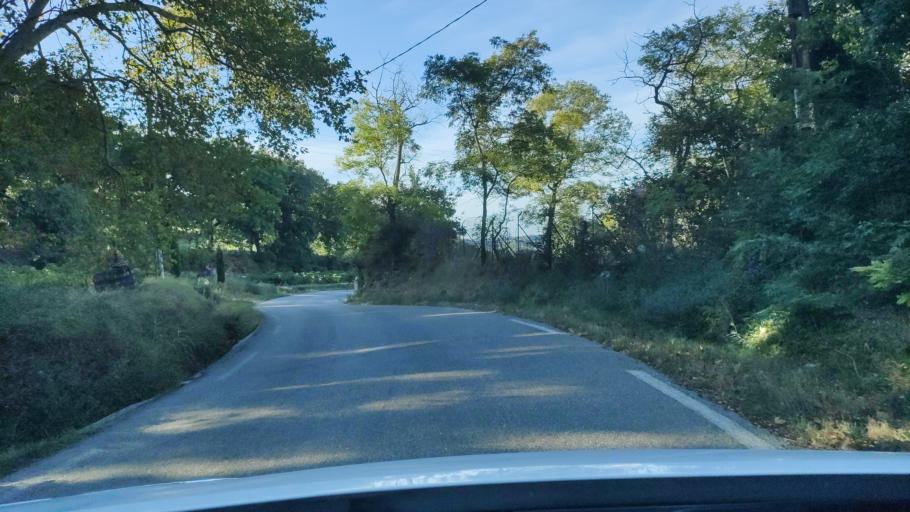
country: FR
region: Languedoc-Roussillon
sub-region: Departement du Gard
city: Saze
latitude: 43.9501
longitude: 4.6561
